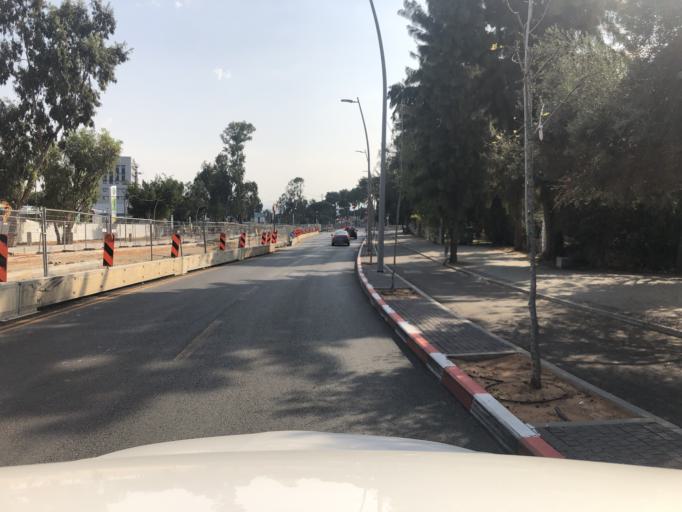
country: IL
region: Central District
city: Kfar Saba
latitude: 32.1718
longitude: 34.9228
